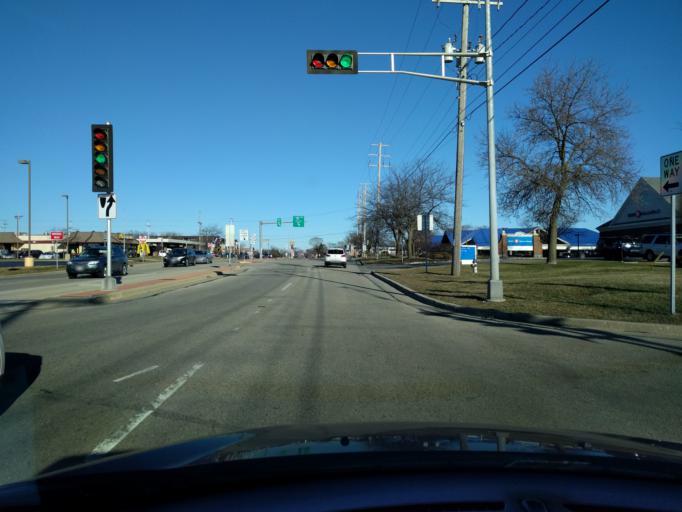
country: US
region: Wisconsin
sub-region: Milwaukee County
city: River Hills
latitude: 43.1751
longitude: -87.9126
